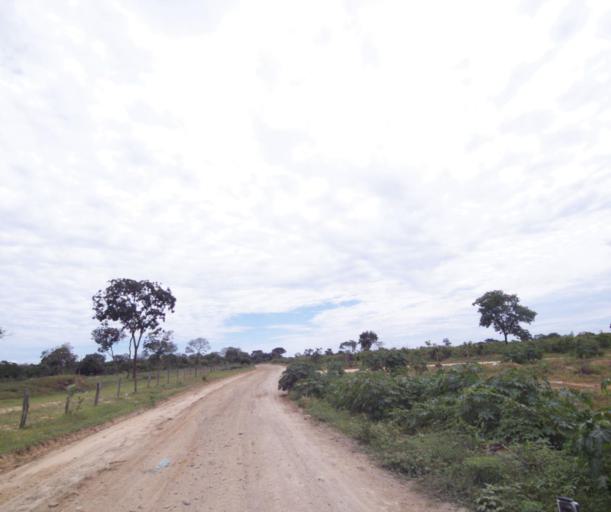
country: BR
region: Bahia
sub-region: Carinhanha
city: Carinhanha
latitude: -14.2291
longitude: -44.3037
